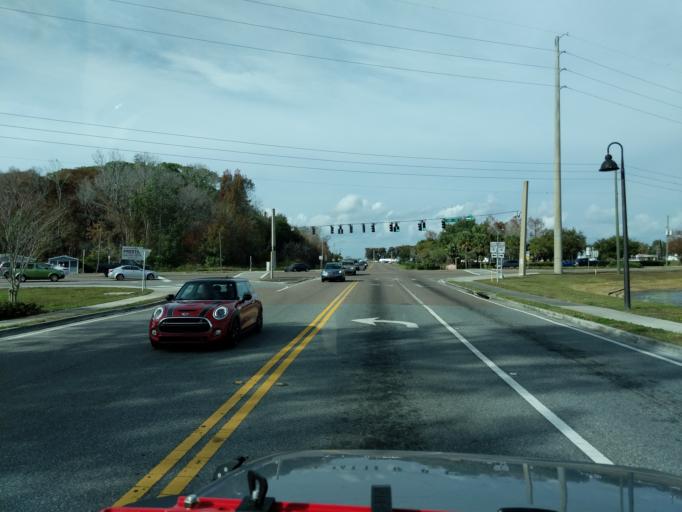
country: US
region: Florida
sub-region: Lake County
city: Tavares
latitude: 28.8066
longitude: -81.7348
